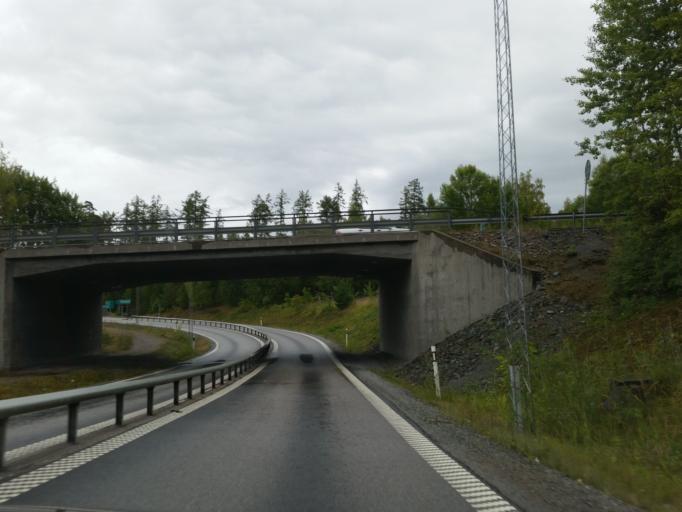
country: SE
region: Uppsala
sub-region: Enkopings Kommun
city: Dalby
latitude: 59.6196
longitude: 17.3915
